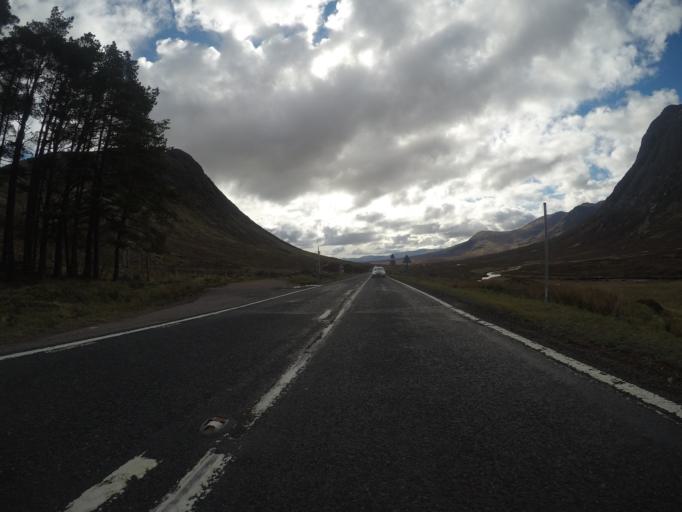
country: GB
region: Scotland
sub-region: Highland
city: Spean Bridge
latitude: 56.6644
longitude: -4.9020
